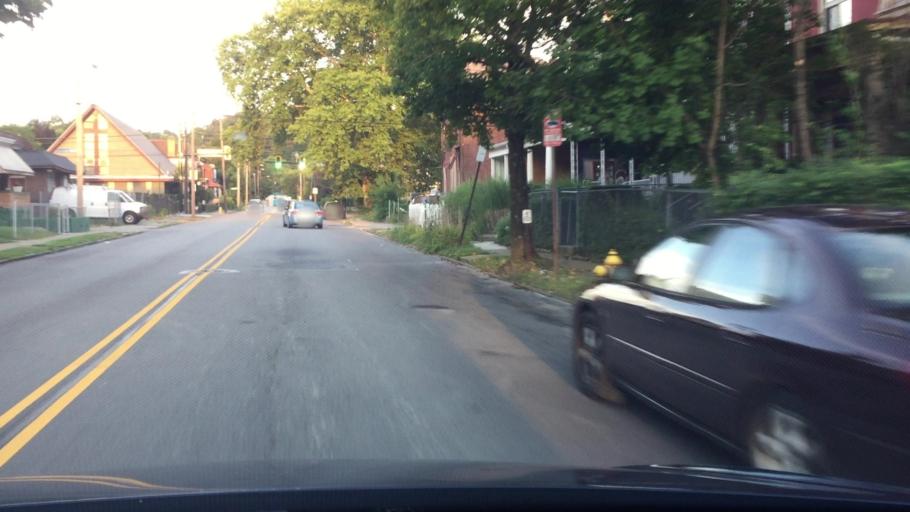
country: US
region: Pennsylvania
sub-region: Allegheny County
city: Wilkinsburg
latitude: 40.4549
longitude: -79.8896
